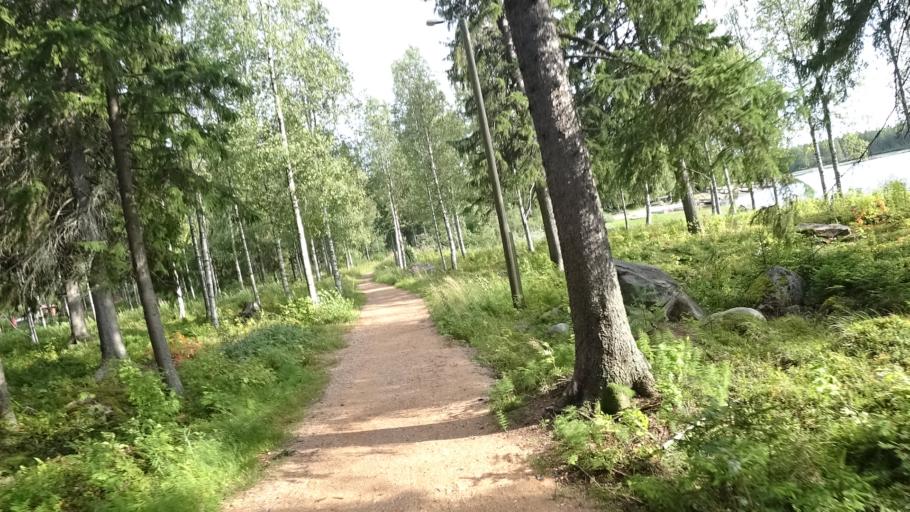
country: FI
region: North Karelia
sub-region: Joensuu
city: Ilomantsi
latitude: 62.6668
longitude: 30.9112
